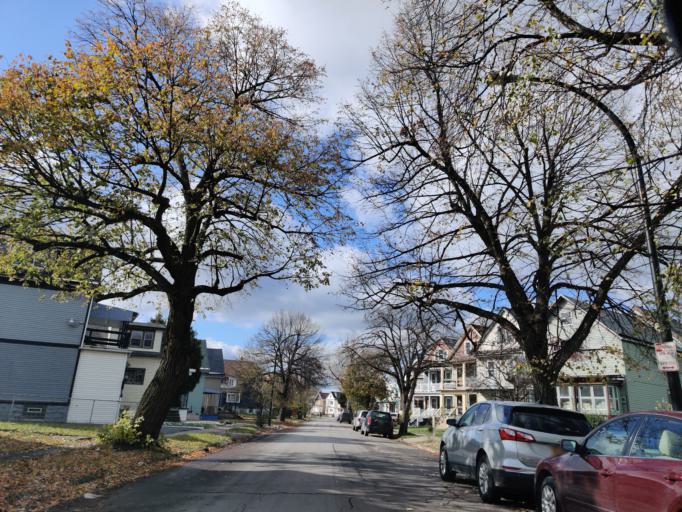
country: US
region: New York
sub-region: Erie County
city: Buffalo
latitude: 42.9114
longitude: -78.8880
